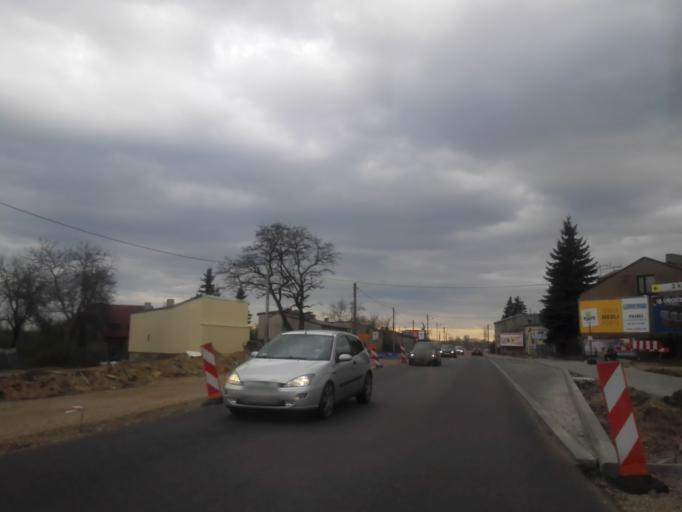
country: PL
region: Silesian Voivodeship
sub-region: Czestochowa
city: Czestochowa
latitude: 50.8335
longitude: 19.1503
